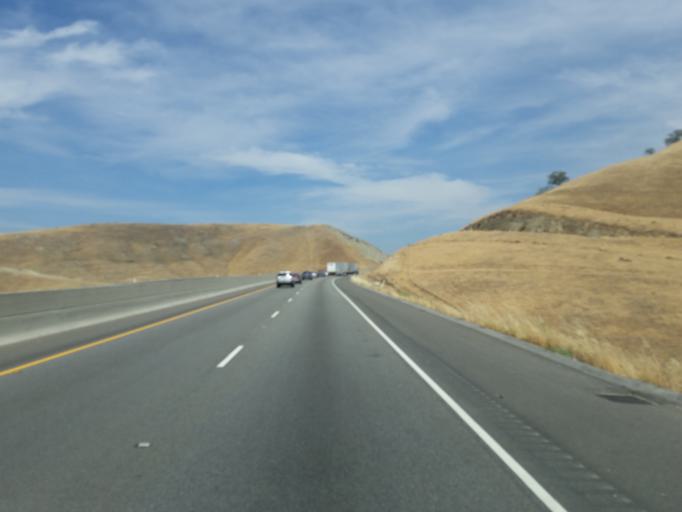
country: US
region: California
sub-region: Kern County
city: Bear Valley Springs
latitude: 35.2699
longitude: -118.6817
